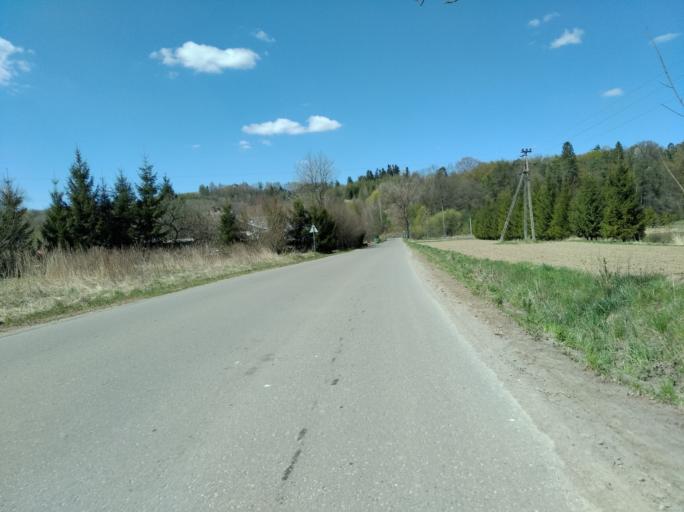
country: PL
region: Subcarpathian Voivodeship
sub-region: Powiat brzozowski
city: Dydnia
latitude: 49.6971
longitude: 22.1955
